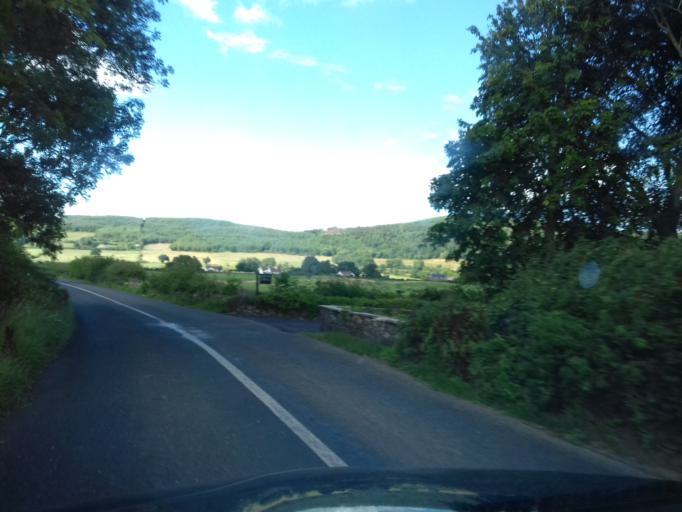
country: IE
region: Munster
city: Carrick-on-Suir
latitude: 52.3900
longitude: -7.4678
